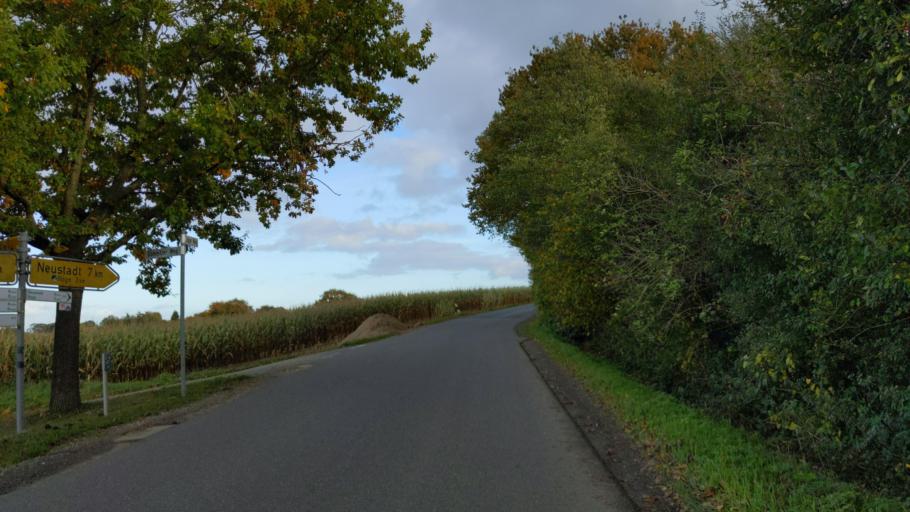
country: DE
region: Schleswig-Holstein
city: Susel
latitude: 54.1035
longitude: 10.7213
